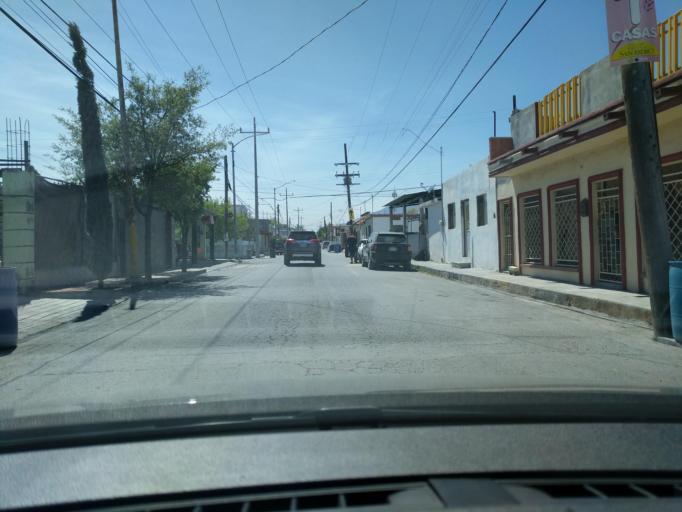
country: MX
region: Nuevo Leon
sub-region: Salinas Victoria
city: Las Torres
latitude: 25.9629
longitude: -100.2984
